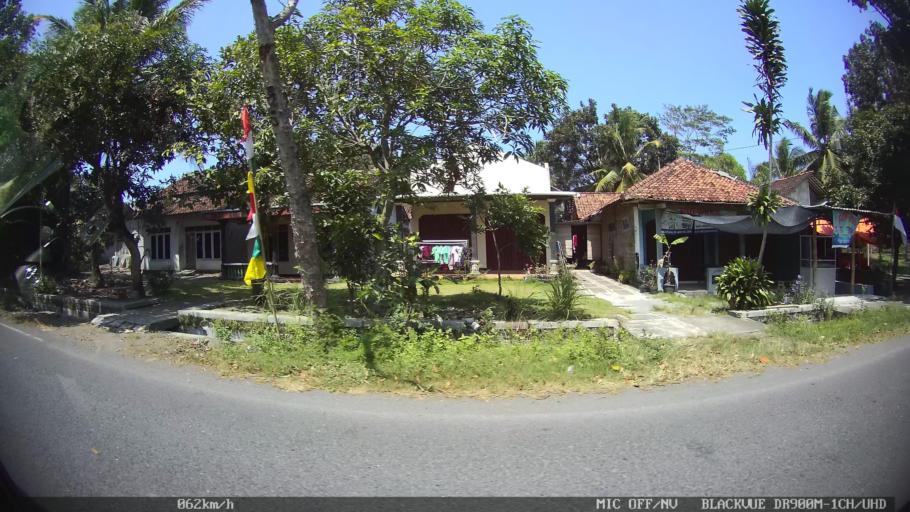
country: ID
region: Daerah Istimewa Yogyakarta
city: Srandakan
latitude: -7.9118
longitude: 110.0909
